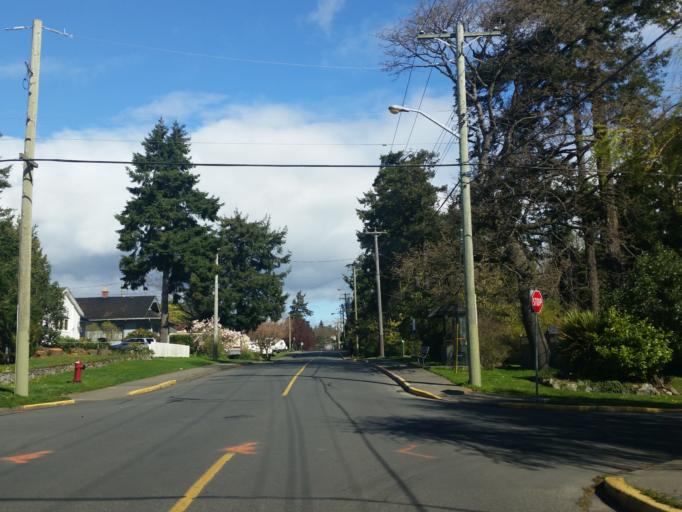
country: CA
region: British Columbia
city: Victoria
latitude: 48.4235
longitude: -123.4087
